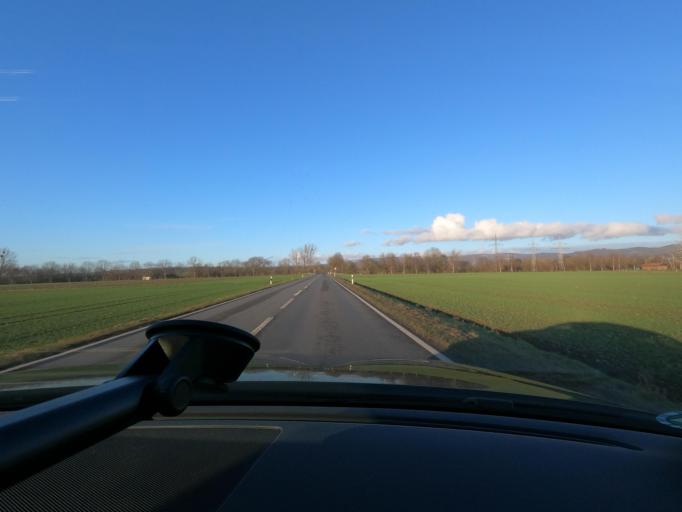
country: DE
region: Lower Saxony
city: Rhumspringe
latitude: 51.6176
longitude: 10.3220
